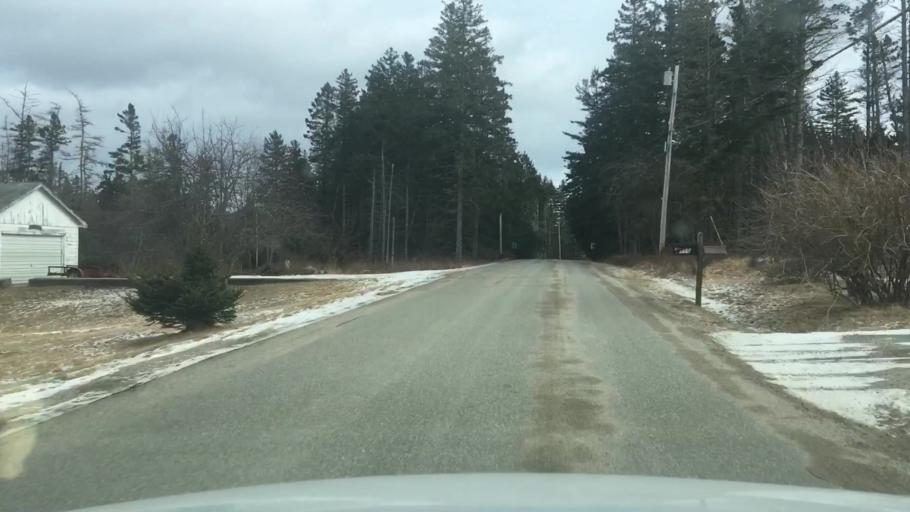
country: US
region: Maine
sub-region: Washington County
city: Machias
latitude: 44.6090
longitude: -67.4725
